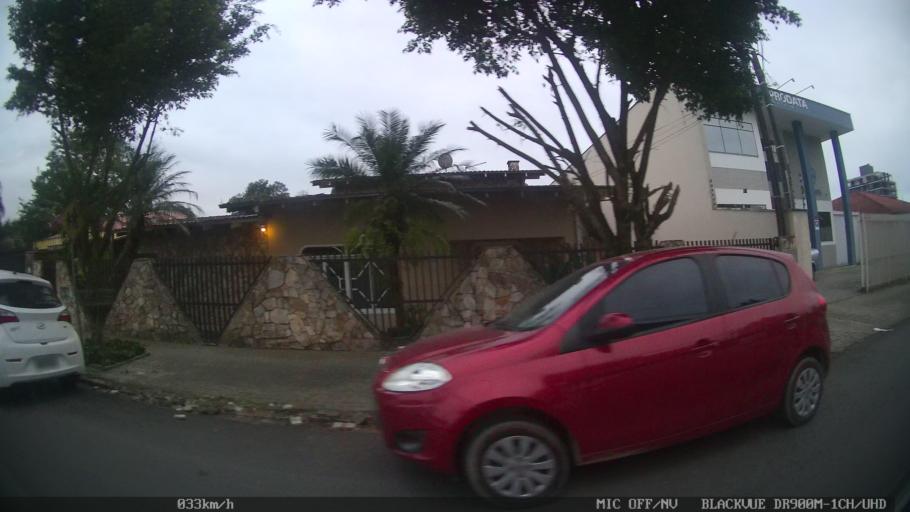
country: BR
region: Santa Catarina
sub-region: Joinville
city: Joinville
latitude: -26.2778
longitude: -48.8558
